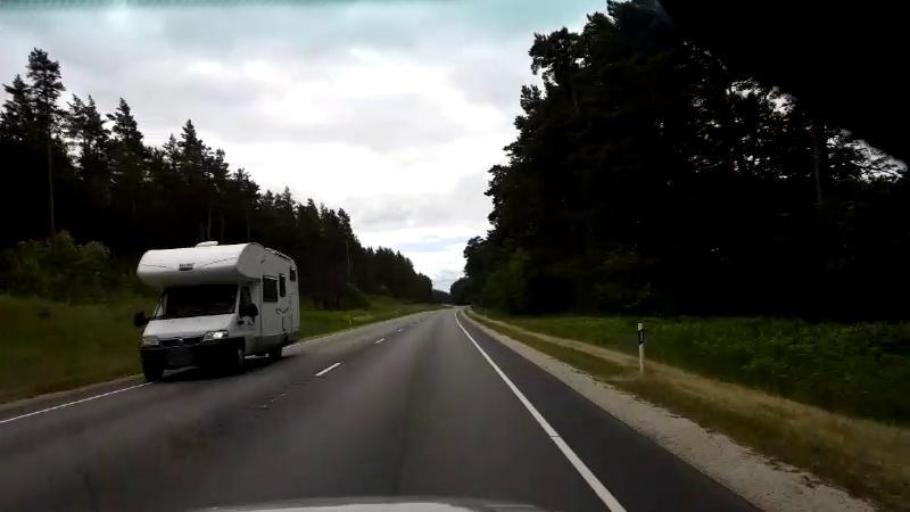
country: EE
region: Paernumaa
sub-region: Paernu linn
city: Parnu
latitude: 58.1679
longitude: 24.4960
